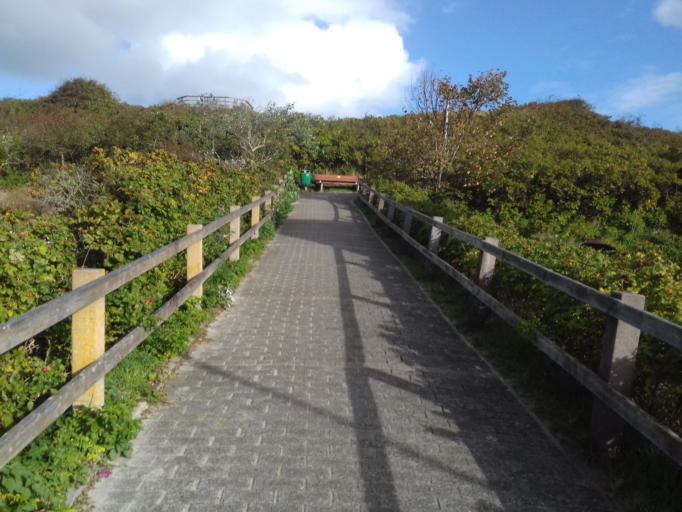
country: DE
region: Lower Saxony
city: Juist
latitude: 53.6767
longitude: 6.9625
